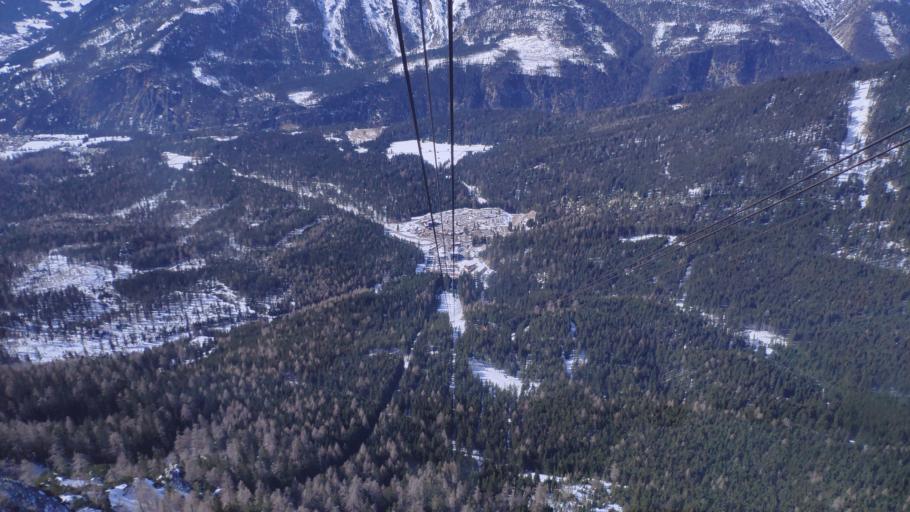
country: AT
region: Tyrol
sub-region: Politischer Bezirk Reutte
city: Ehrwald
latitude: 47.4244
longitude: 10.9603
